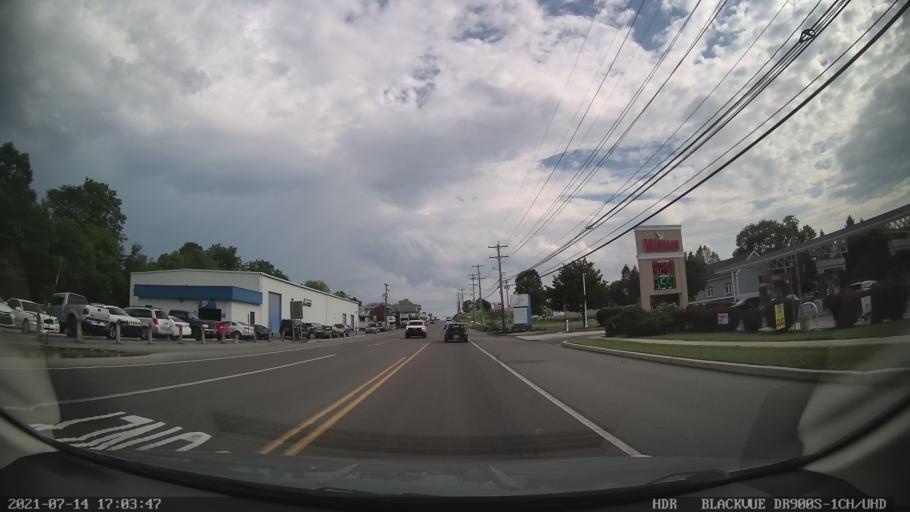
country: US
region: Pennsylvania
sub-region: Berks County
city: Muhlenberg Park
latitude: 40.3894
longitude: -75.9350
